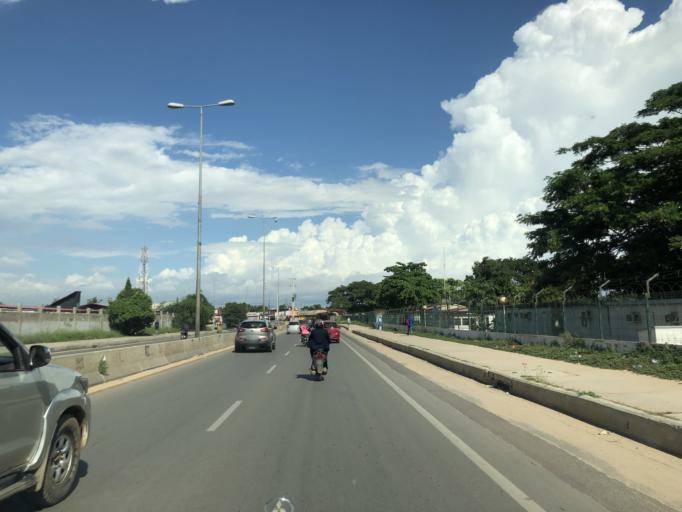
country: AO
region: Luanda
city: Luanda
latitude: -8.8947
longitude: 13.2127
